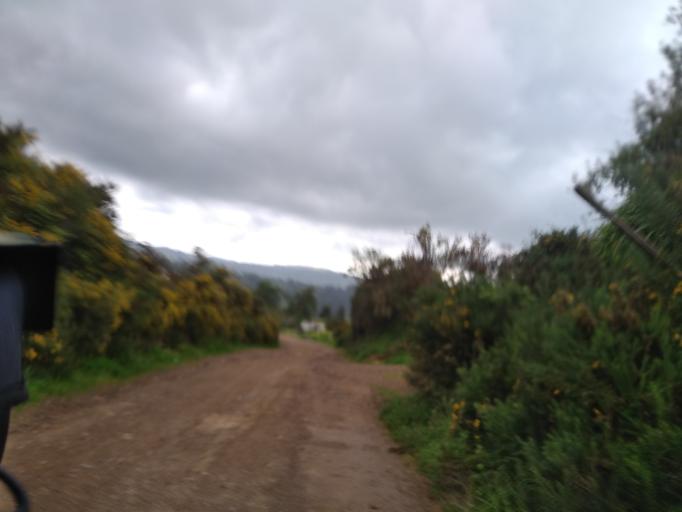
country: CO
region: Boyaca
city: Sotaquira
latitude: 5.7678
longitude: -73.2588
